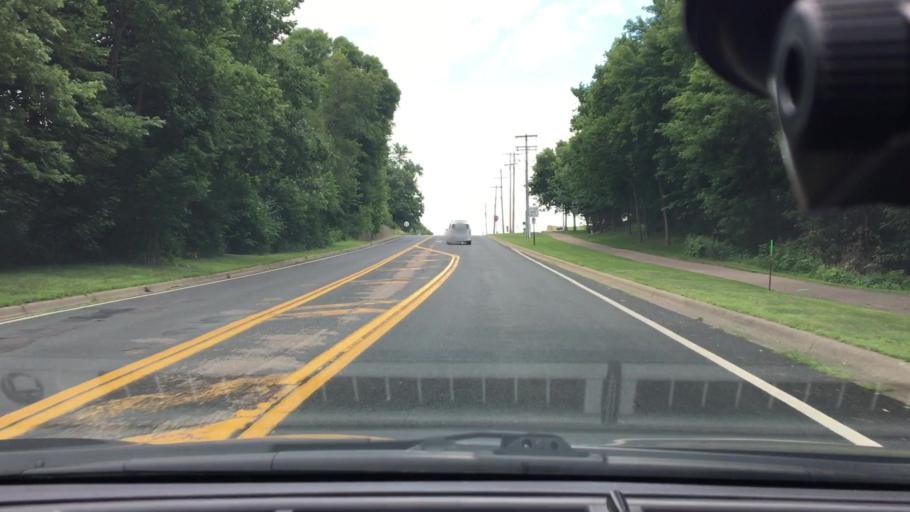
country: US
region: Minnesota
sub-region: Hennepin County
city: Plymouth
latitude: 45.0231
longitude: -93.4209
